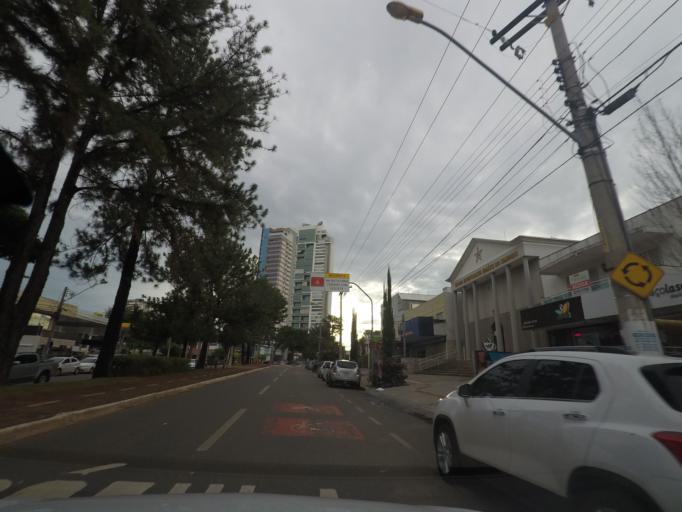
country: BR
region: Goias
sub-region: Goiania
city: Goiania
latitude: -16.7040
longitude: -49.2599
